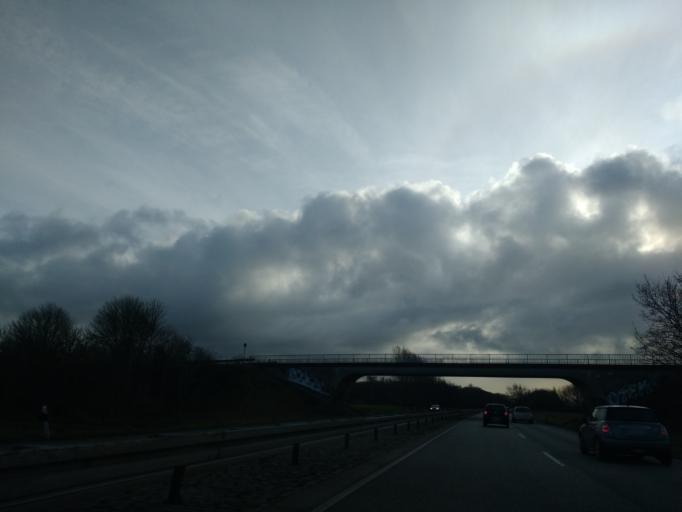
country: DE
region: Schleswig-Holstein
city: Neumunster
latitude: 54.1110
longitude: 9.9676
